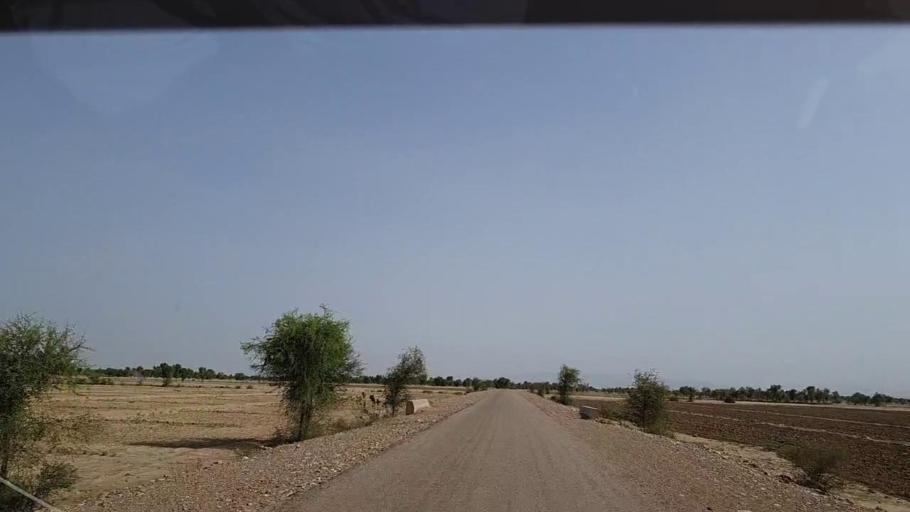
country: PK
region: Sindh
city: Johi
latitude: 26.6521
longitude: 67.5049
